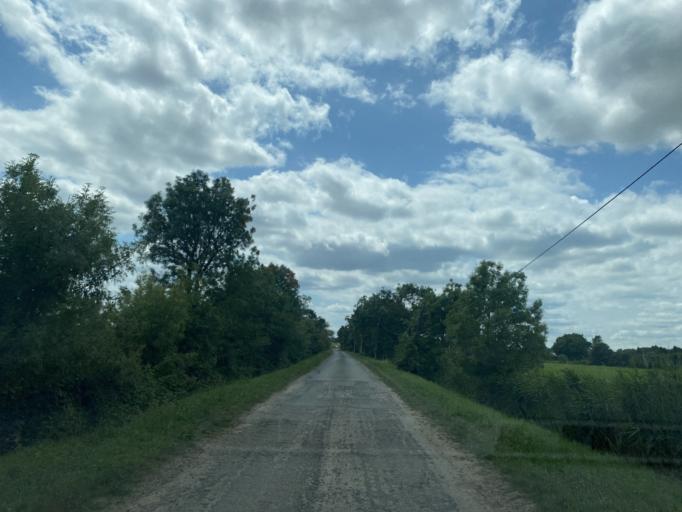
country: FR
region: Aquitaine
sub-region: Departement de la Gironde
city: Soussans
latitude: 45.0639
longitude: -0.6775
